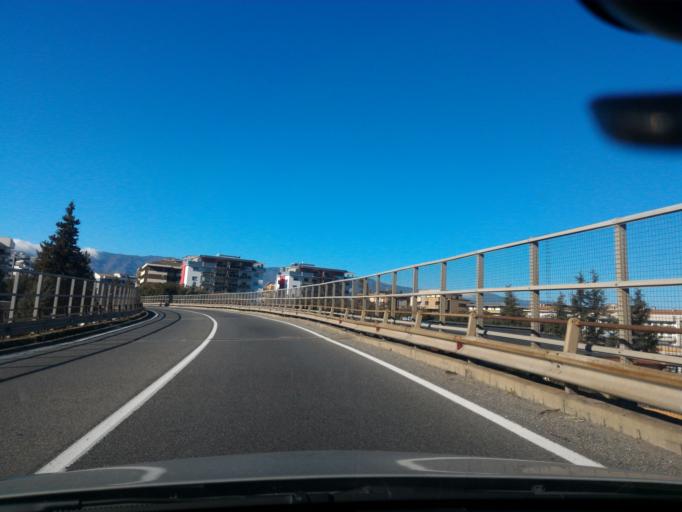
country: IT
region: Calabria
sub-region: Provincia di Cosenza
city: Quattromiglia
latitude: 39.3321
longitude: 16.2440
